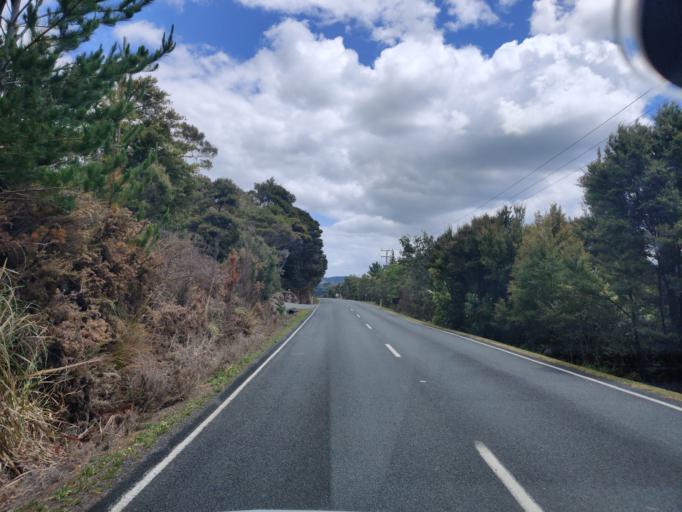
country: NZ
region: Northland
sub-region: Far North District
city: Paihia
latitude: -35.3037
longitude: 174.1271
